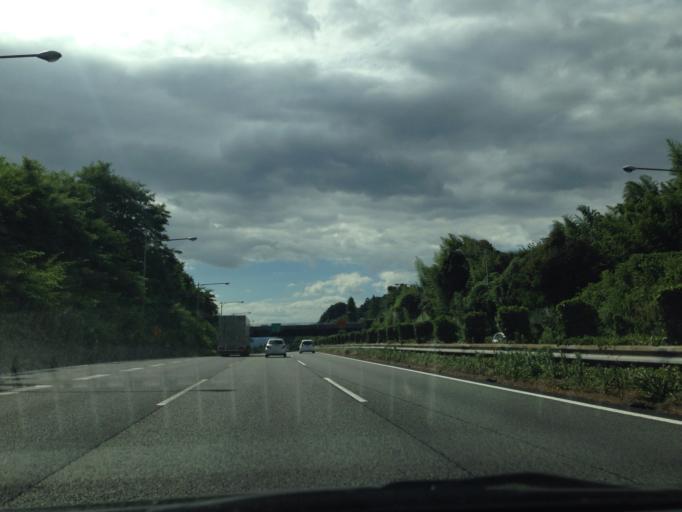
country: JP
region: Kanagawa
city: Hadano
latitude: 35.3386
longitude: 139.1752
